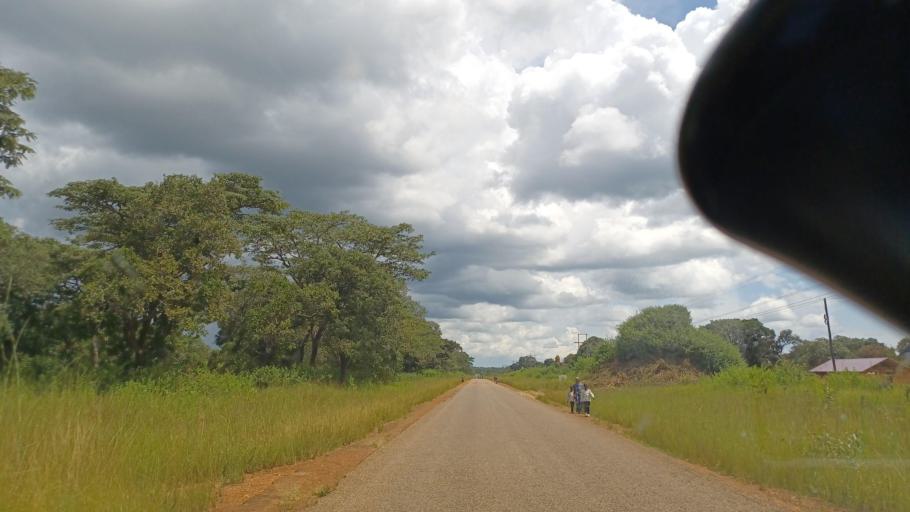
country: ZM
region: North-Western
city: Solwezi
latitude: -12.7661
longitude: 26.0180
